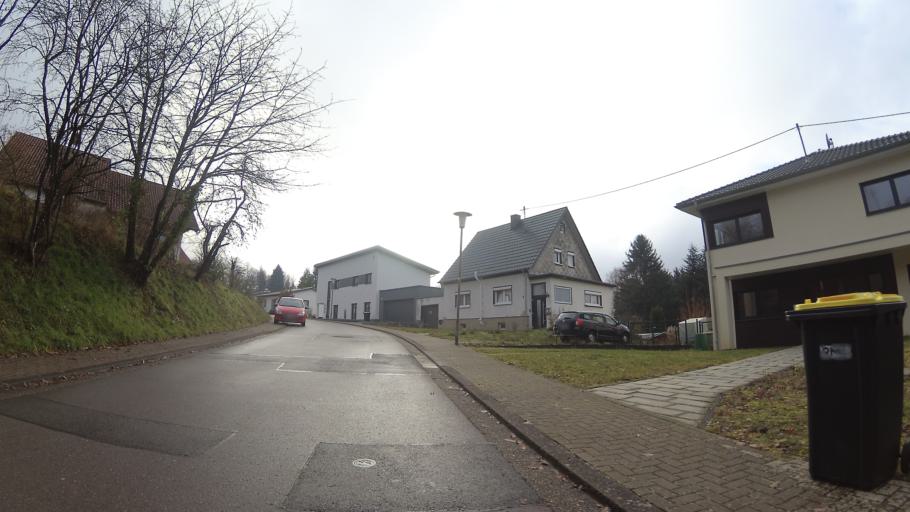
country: DE
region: Saarland
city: Spiesen-Elversberg
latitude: 49.3127
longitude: 7.1622
